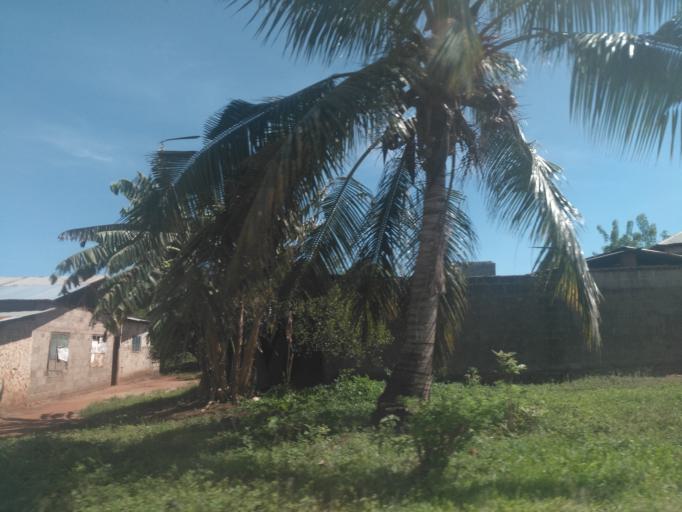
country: TZ
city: Kiwengwa
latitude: -5.9872
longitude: 39.3335
